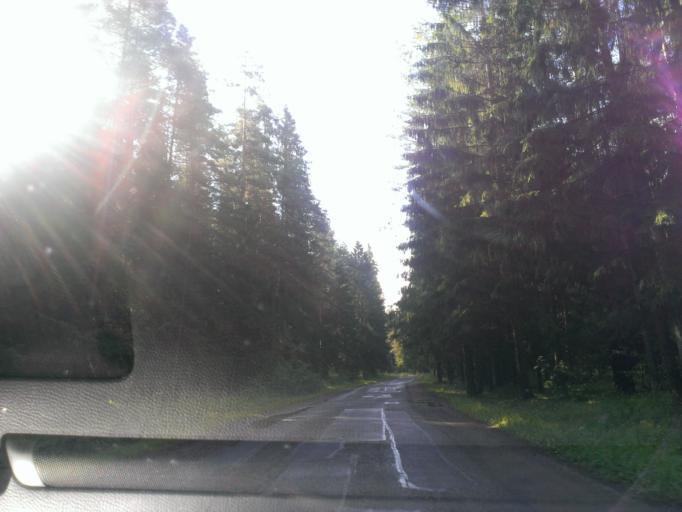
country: LV
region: Incukalns
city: Vangazi
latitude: 57.0982
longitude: 24.5337
